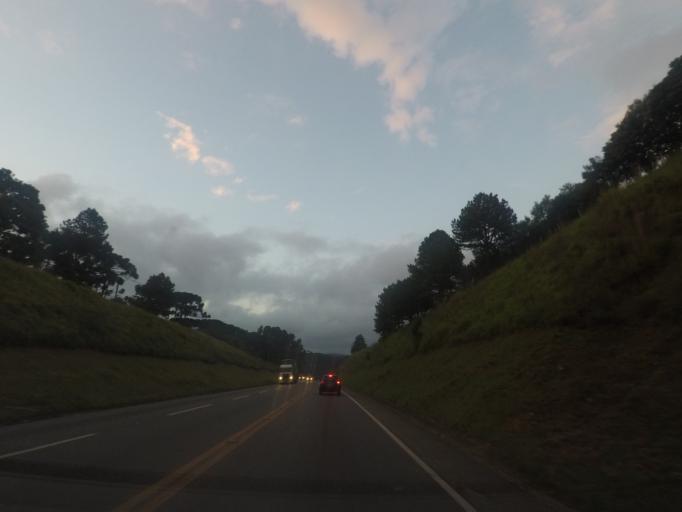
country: BR
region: Parana
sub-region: Almirante Tamandare
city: Almirante Tamandare
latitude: -25.4009
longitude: -49.3616
